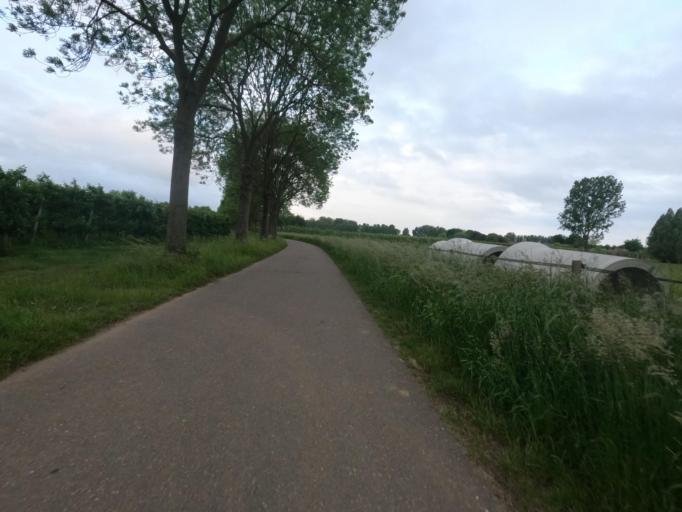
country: NL
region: Limburg
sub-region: Gemeente Roerdalen
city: Vlodrop
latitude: 51.1352
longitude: 6.0903
